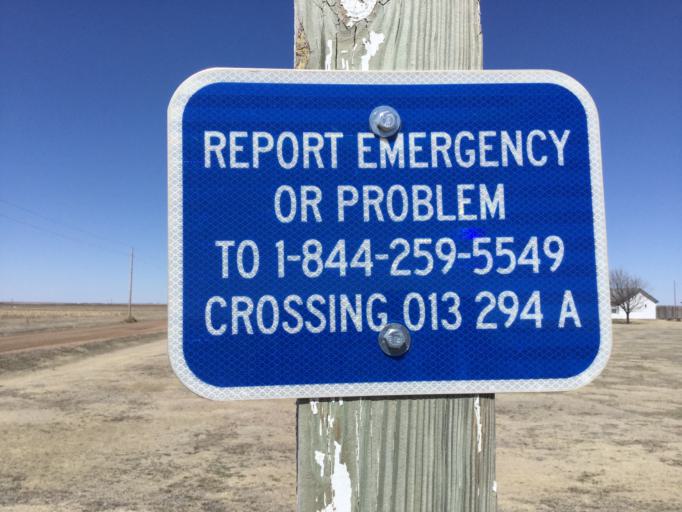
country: US
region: Kansas
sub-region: Grant County
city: Ulysses
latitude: 37.5909
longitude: -101.2902
